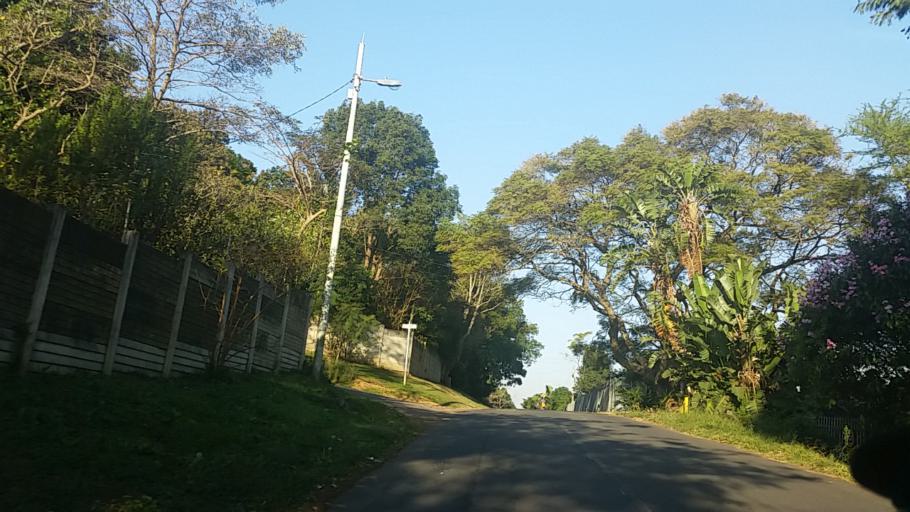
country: ZA
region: KwaZulu-Natal
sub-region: eThekwini Metropolitan Municipality
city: Berea
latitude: -29.8364
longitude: 30.9092
